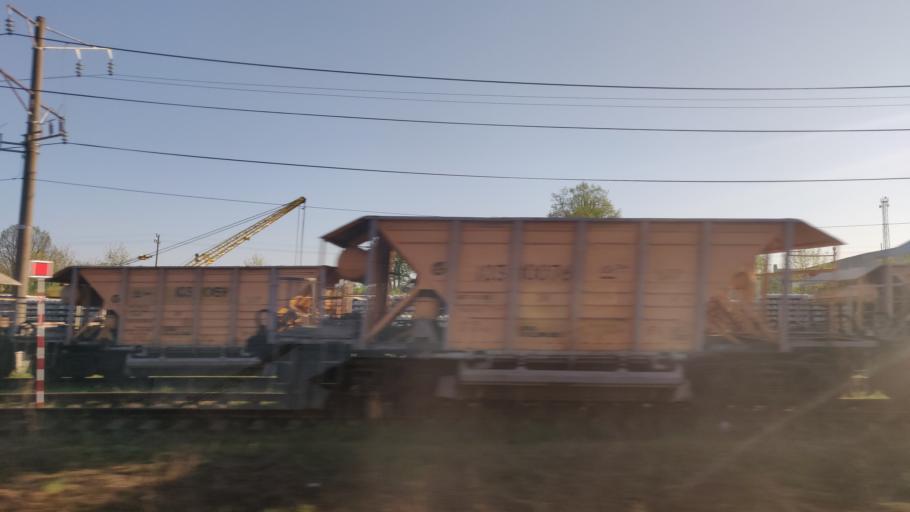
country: LT
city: Lentvaris
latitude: 54.6435
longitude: 25.0636
